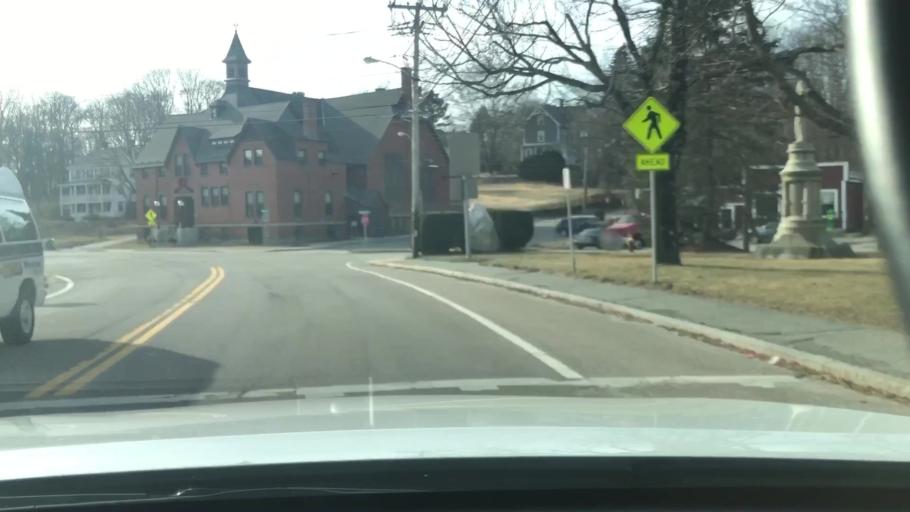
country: US
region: Massachusetts
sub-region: Worcester County
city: Upton
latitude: 42.1741
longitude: -71.6027
